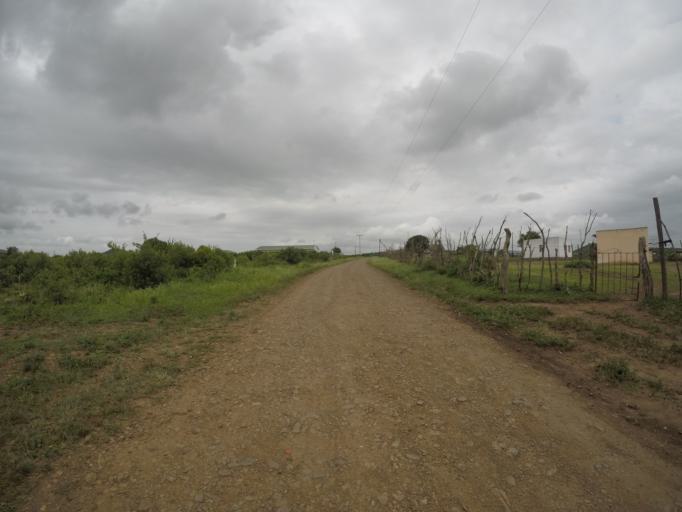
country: ZA
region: KwaZulu-Natal
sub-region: uThungulu District Municipality
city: Empangeni
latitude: -28.5976
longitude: 31.8315
